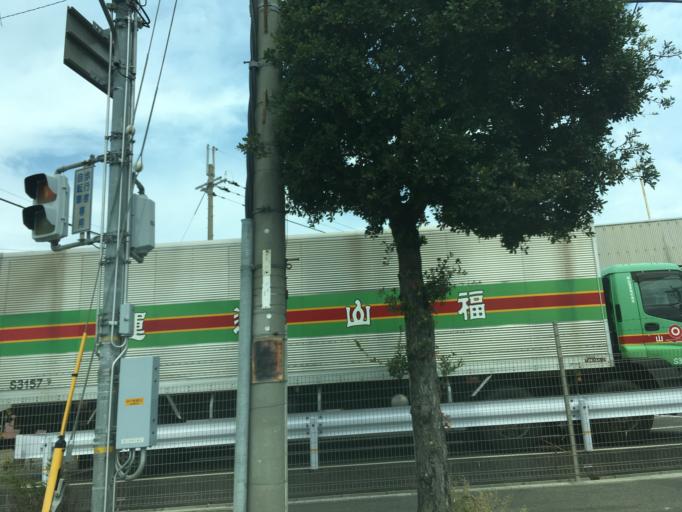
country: JP
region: Hyogo
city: Ashiya
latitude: 34.7171
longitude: 135.2953
